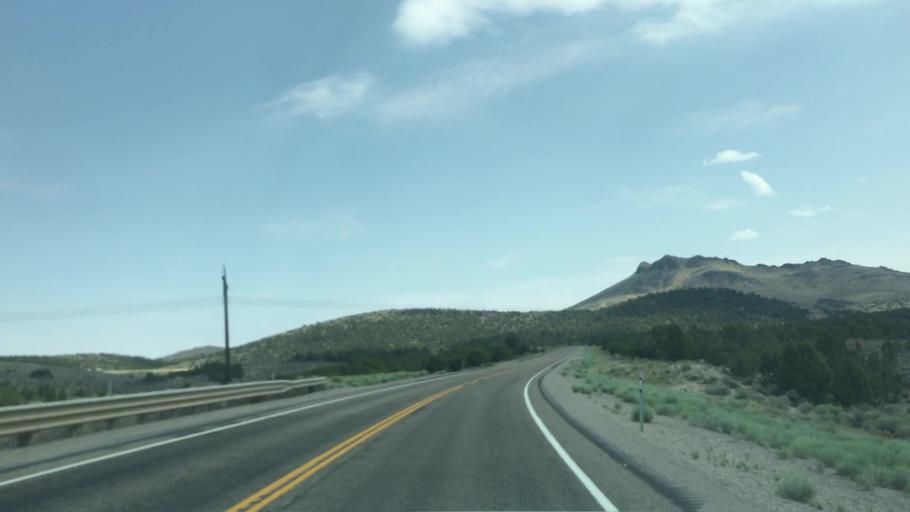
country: US
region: Nevada
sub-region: White Pine County
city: Ely
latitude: 39.4028
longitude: -115.0822
